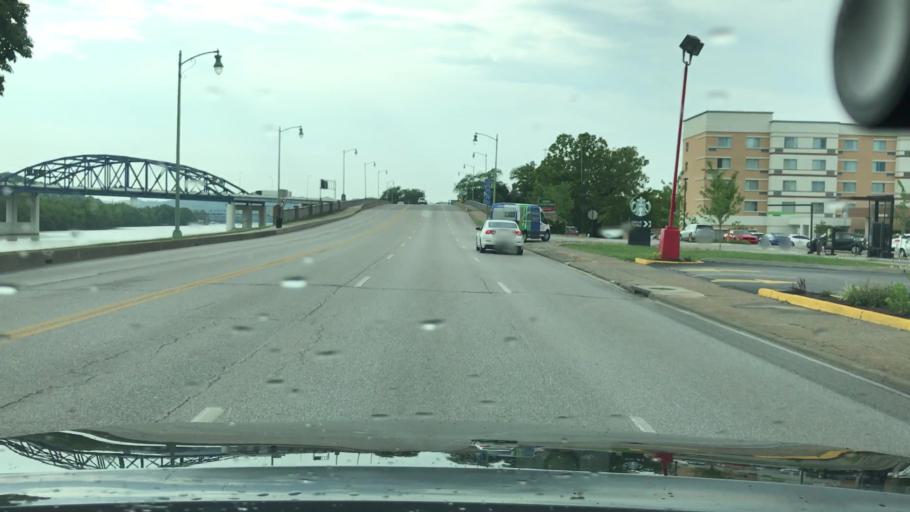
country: US
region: West Virginia
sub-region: Kanawha County
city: Charleston
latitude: 38.3534
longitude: -81.6431
